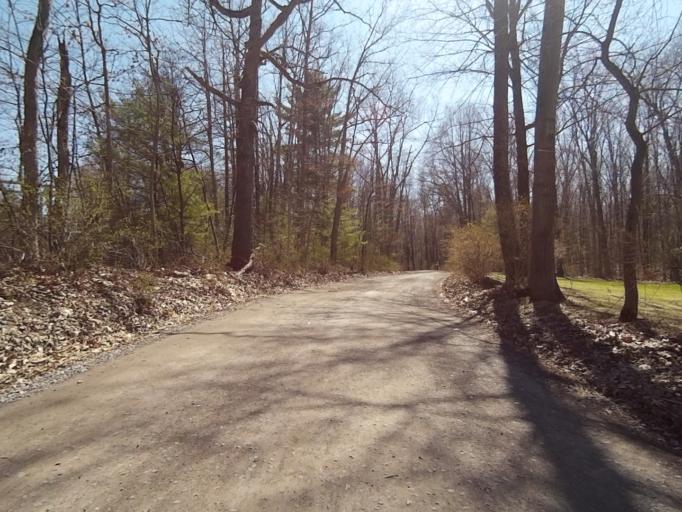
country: US
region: Pennsylvania
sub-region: Centre County
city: Park Forest Village
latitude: 40.8068
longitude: -77.9447
